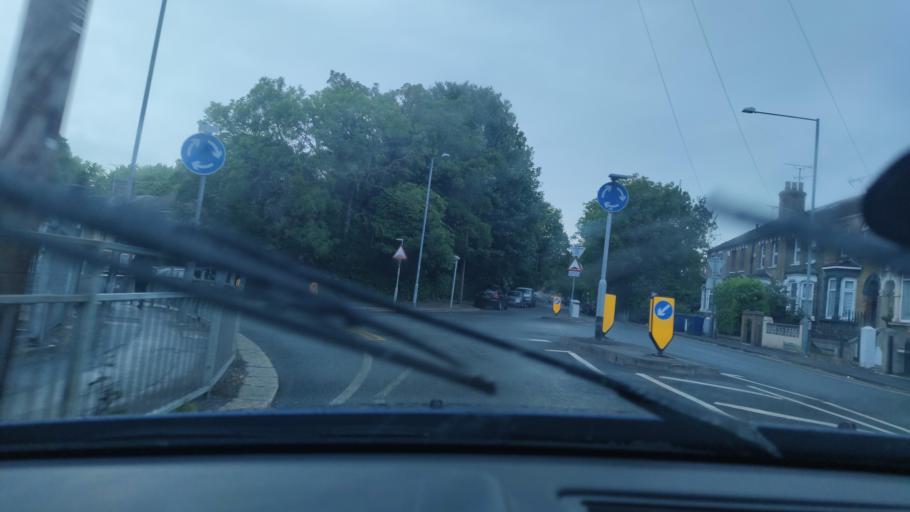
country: GB
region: England
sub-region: Borough of Thurrock
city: Grays
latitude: 51.4774
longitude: 0.3306
